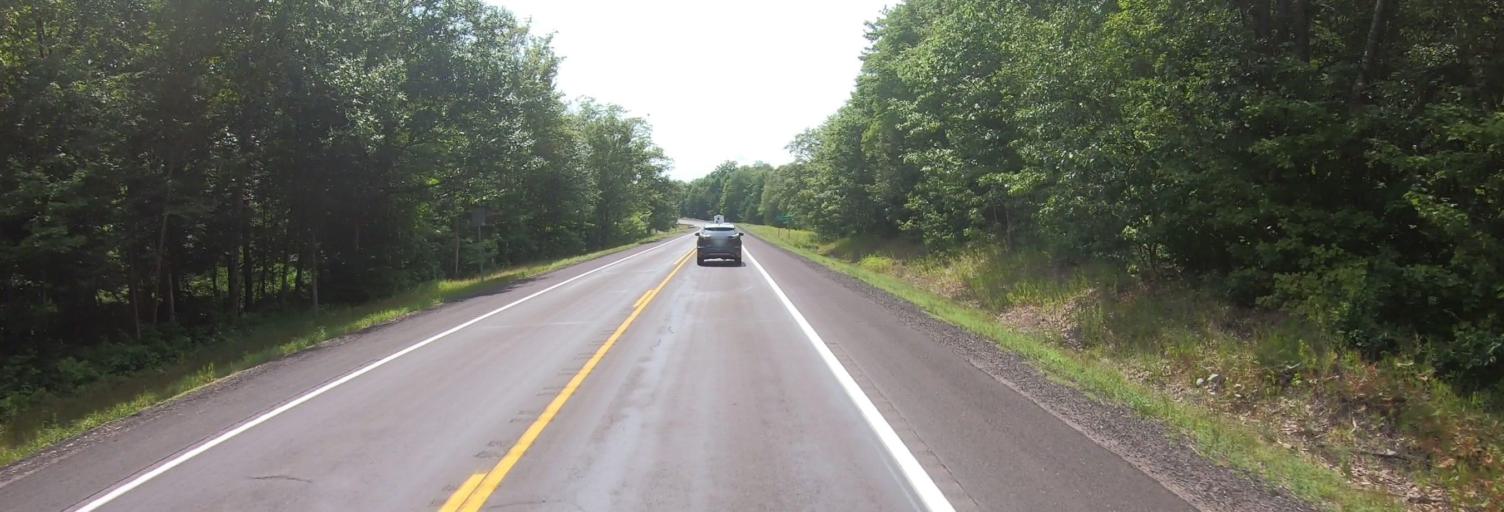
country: US
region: Michigan
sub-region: Houghton County
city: Hancock
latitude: 46.8978
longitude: -88.8489
